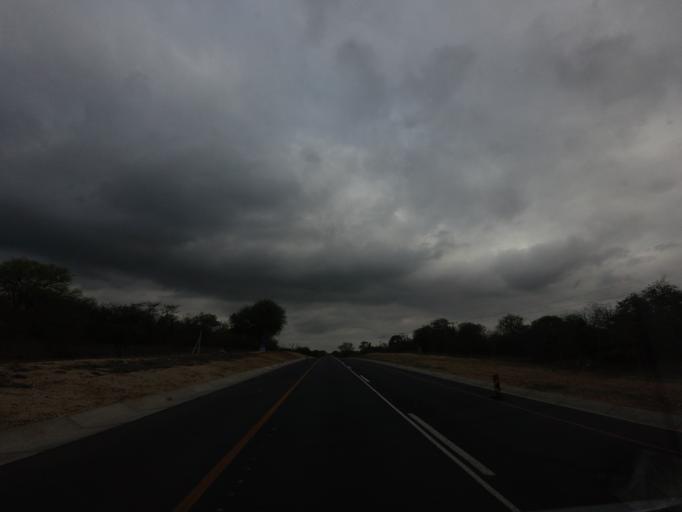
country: ZA
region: Mpumalanga
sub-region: Ehlanzeni District
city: Komatipoort
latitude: -25.4405
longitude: 31.7473
